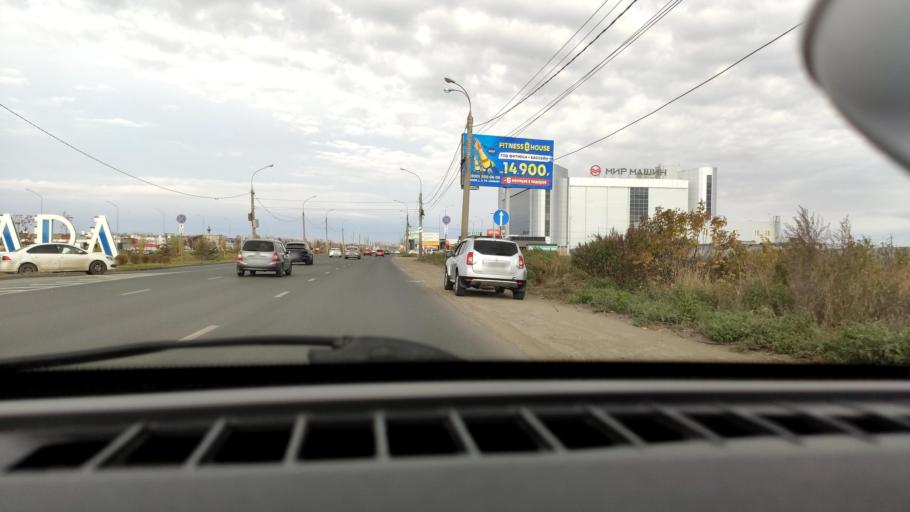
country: RU
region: Samara
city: Samara
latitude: 53.1335
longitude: 50.1737
